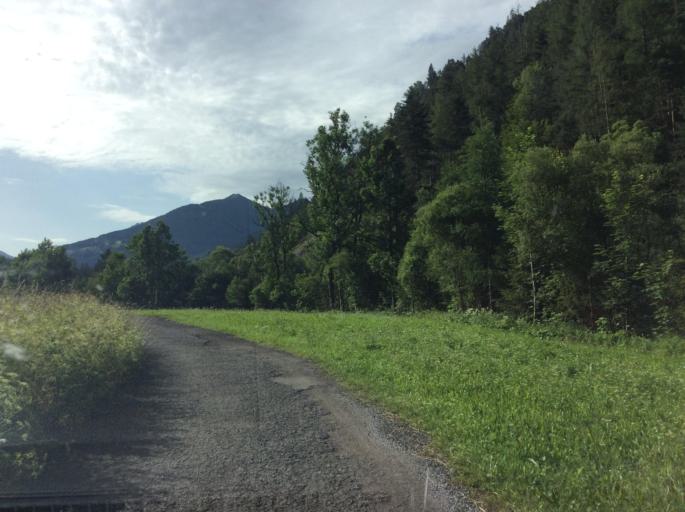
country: AT
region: Salzburg
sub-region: Politischer Bezirk Sankt Johann im Pongau
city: Forstau
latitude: 47.4002
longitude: 13.5794
